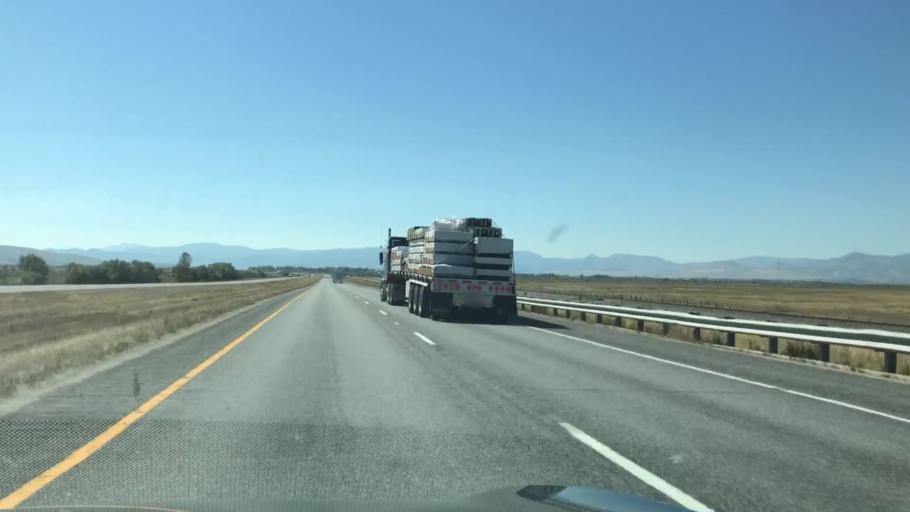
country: US
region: Montana
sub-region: Deer Lodge County
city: Warm Springs
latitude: 46.2079
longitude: -112.7774
